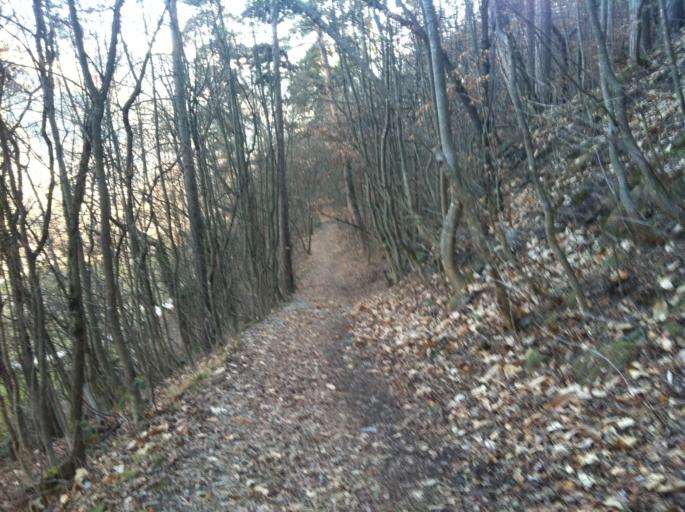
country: IT
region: Trentino-Alto Adige
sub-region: Bolzano
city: Bressanone
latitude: 46.7202
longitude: 11.6668
